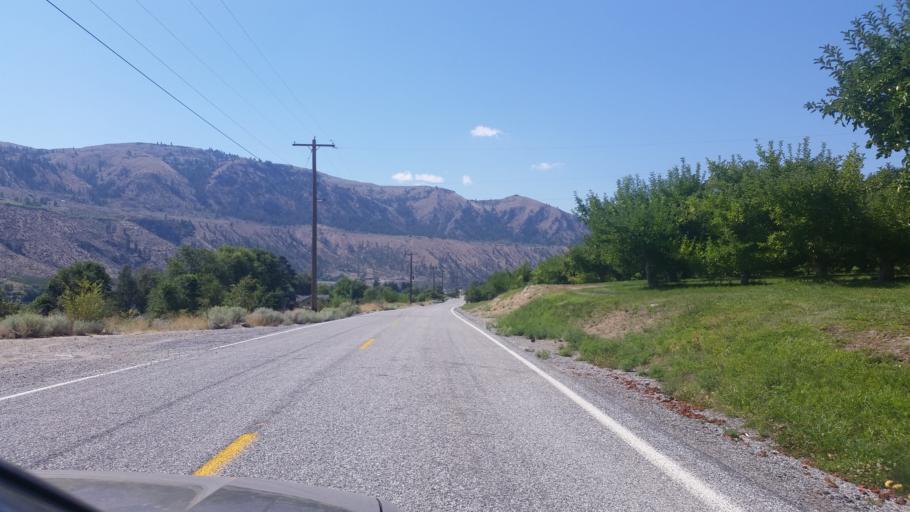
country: US
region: Washington
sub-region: Chelan County
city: Chelan
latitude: 47.7947
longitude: -119.9894
